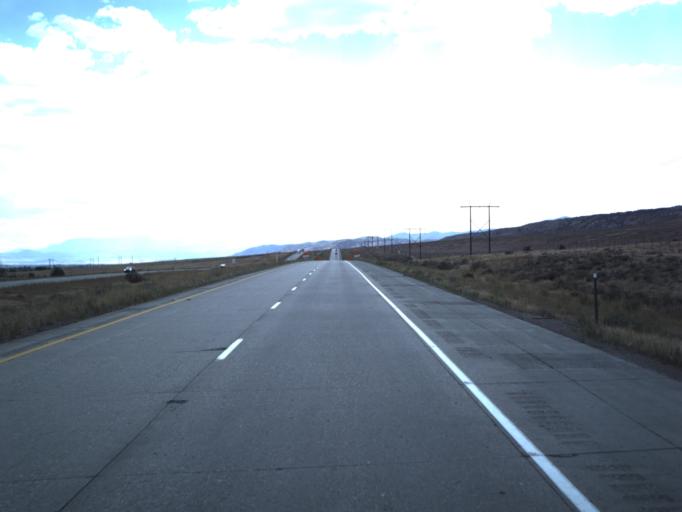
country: US
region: Utah
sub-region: Sevier County
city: Richfield
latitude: 38.8354
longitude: -112.0304
